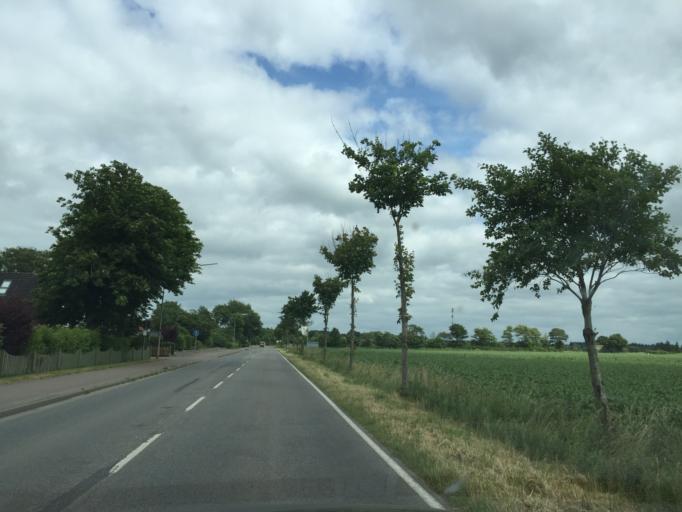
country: DE
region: Schleswig-Holstein
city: Suderlugum
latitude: 54.8690
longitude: 8.8984
